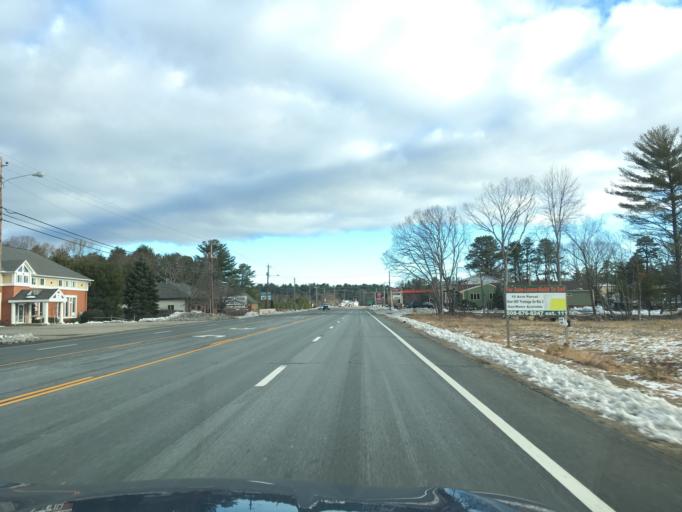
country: US
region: Rhode Island
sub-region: Kent County
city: West Greenwich
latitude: 41.6659
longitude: -71.6014
